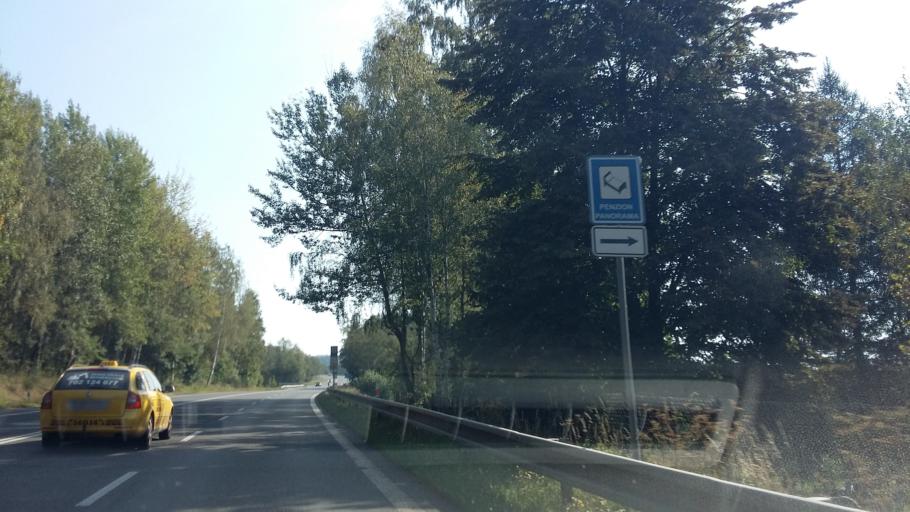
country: CZ
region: Liberecky
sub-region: Okres Jablonec nad Nisou
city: Jablonec nad Nisou
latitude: 50.6898
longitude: 15.1419
